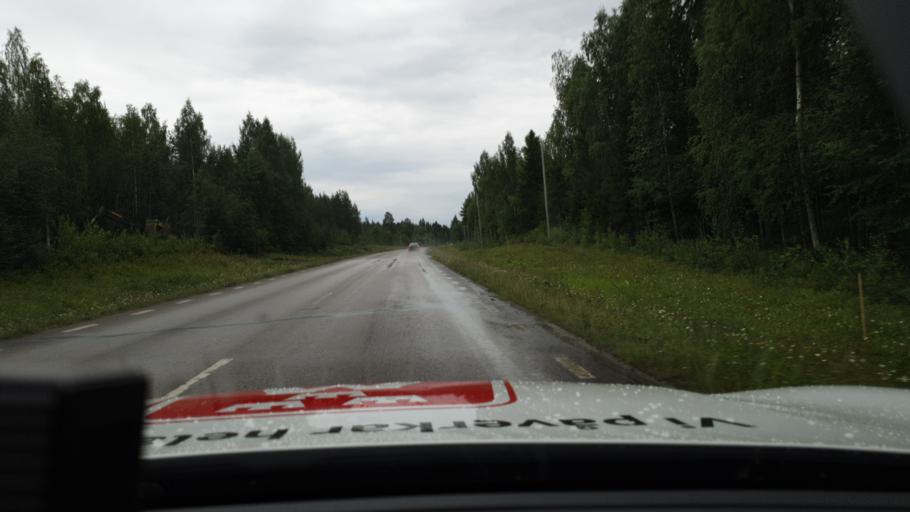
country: SE
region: Norrbotten
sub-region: Alvsbyns Kommun
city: AElvsbyn
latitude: 66.1224
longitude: 20.9200
